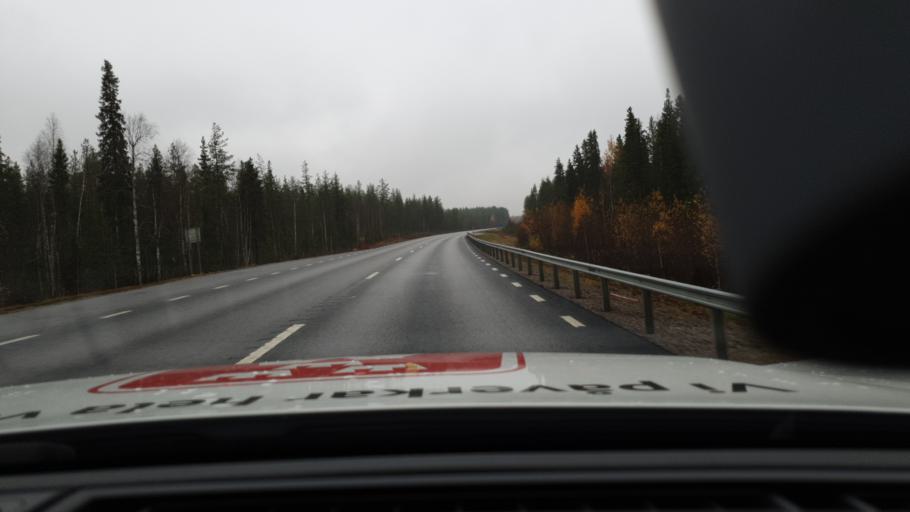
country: SE
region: Norrbotten
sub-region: Overkalix Kommun
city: OEverkalix
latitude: 66.6322
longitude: 22.2082
